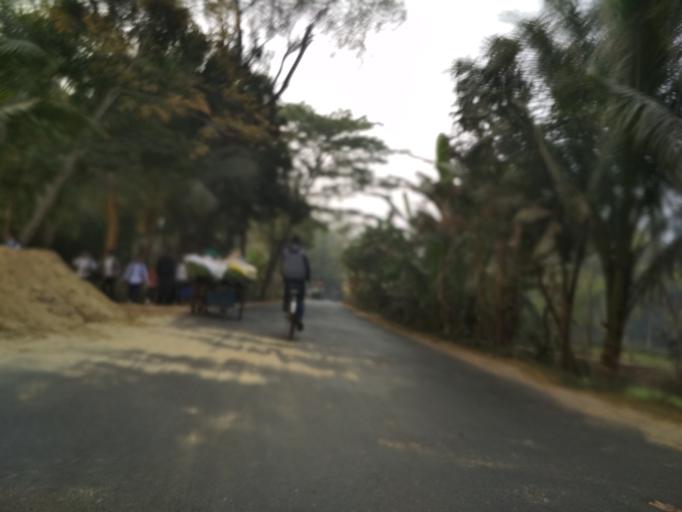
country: BD
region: Chittagong
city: Lakshmipur
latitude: 22.9230
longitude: 90.8353
